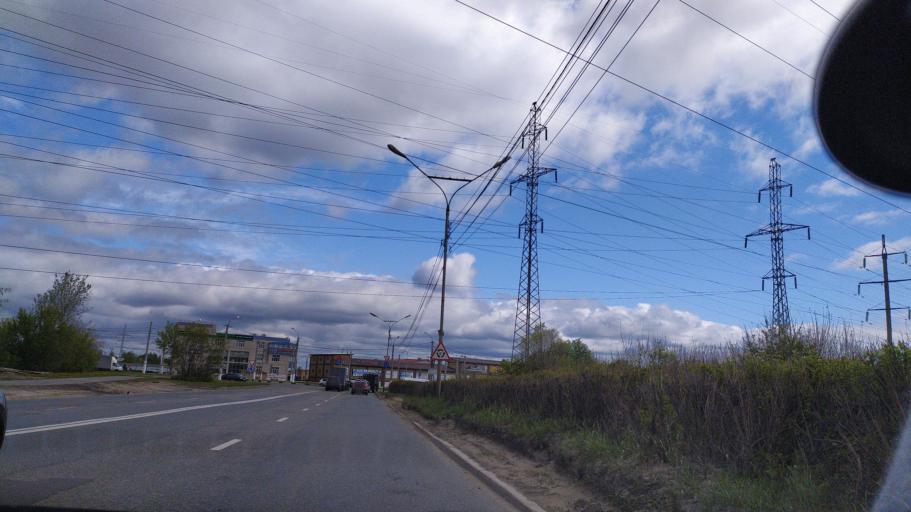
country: RU
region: Chuvashia
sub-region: Cheboksarskiy Rayon
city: Cheboksary
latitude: 56.1268
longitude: 47.3093
